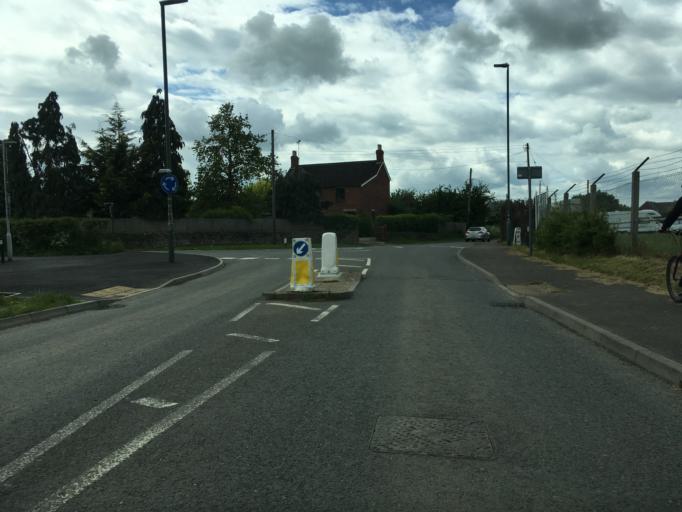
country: GB
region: England
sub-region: Gloucestershire
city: Stonehouse
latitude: 51.7527
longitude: -2.2917
